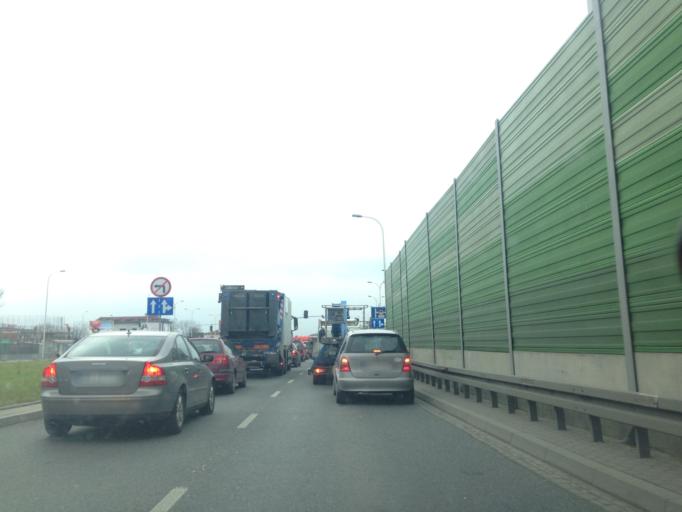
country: PL
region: Masovian Voivodeship
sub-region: Warszawa
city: Rembertow
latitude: 52.2430
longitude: 21.1363
